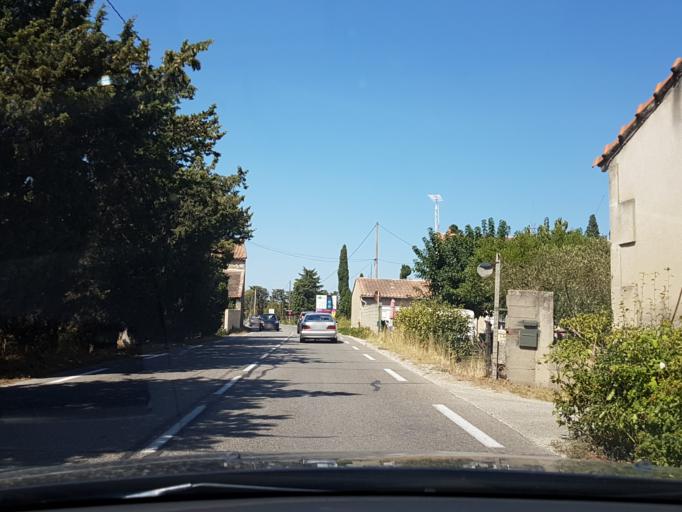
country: FR
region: Provence-Alpes-Cote d'Azur
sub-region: Departement des Bouches-du-Rhone
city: Chateaurenard
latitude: 43.8822
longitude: 4.8314
